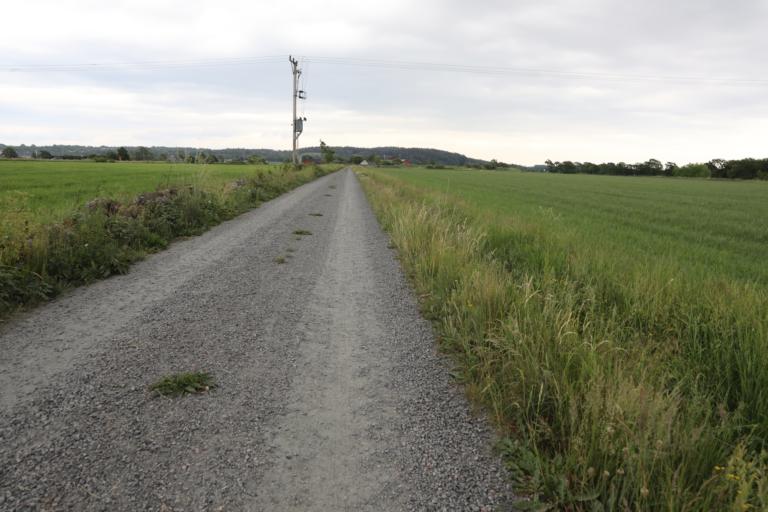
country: SE
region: Halland
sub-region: Varbergs Kommun
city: Varberg
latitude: 57.1623
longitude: 12.2687
